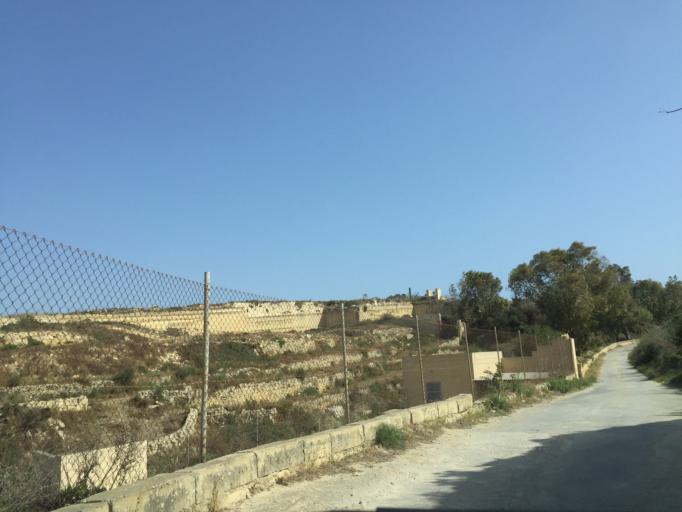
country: MT
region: L-Gharb
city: Gharb
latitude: 36.0693
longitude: 14.2064
